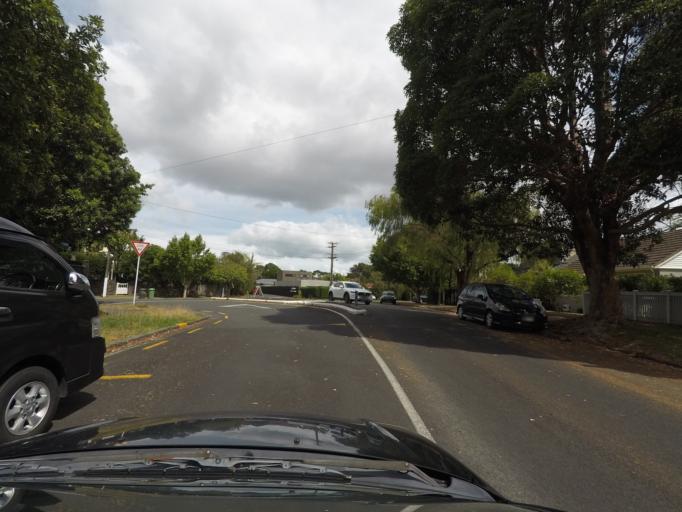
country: NZ
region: Auckland
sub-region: Auckland
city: Rosebank
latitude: -36.8842
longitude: 174.7091
